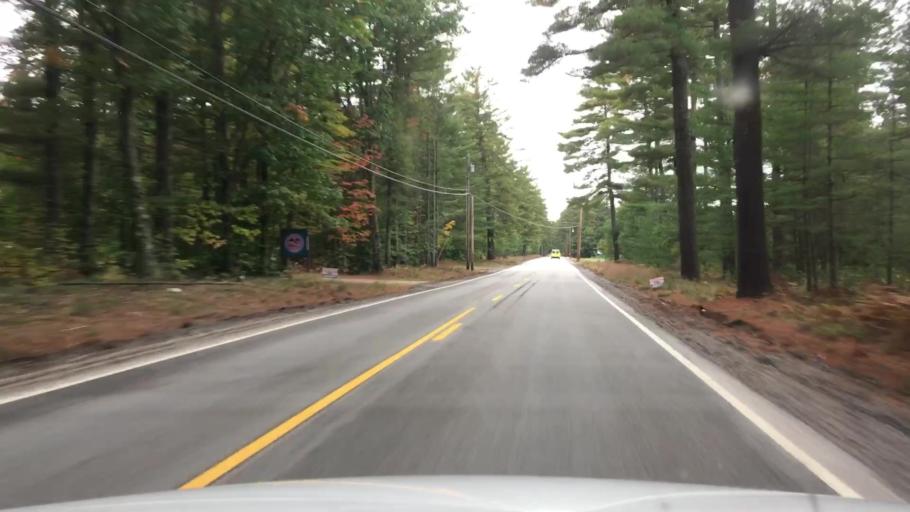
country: US
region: Maine
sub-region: Cumberland County
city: Harrison
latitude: 44.2242
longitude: -70.6973
